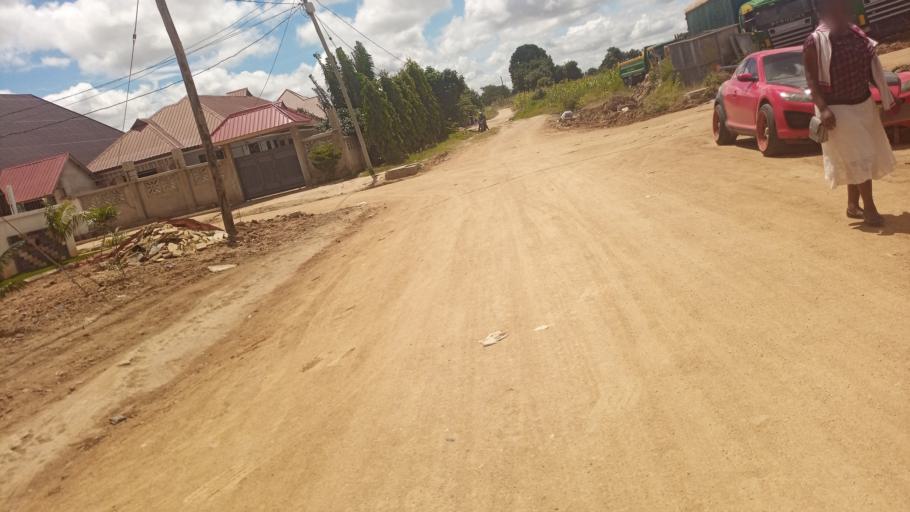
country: TZ
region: Dodoma
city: Dodoma
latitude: -6.1787
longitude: 35.7656
